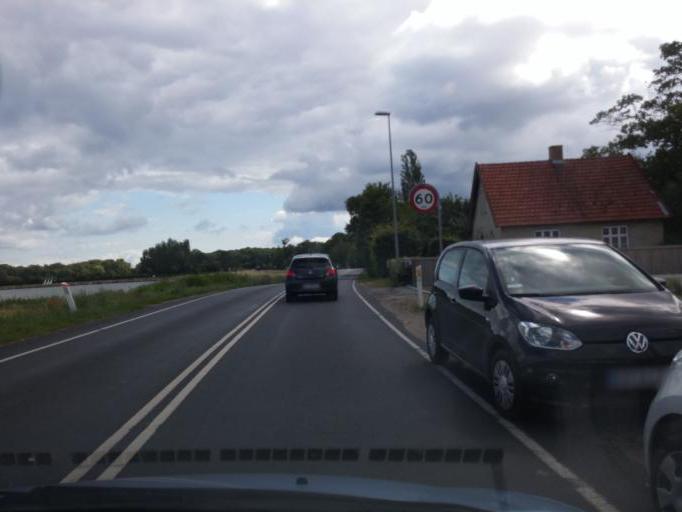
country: DK
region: South Denmark
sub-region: Kerteminde Kommune
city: Kerteminde
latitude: 55.4420
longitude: 10.6508
